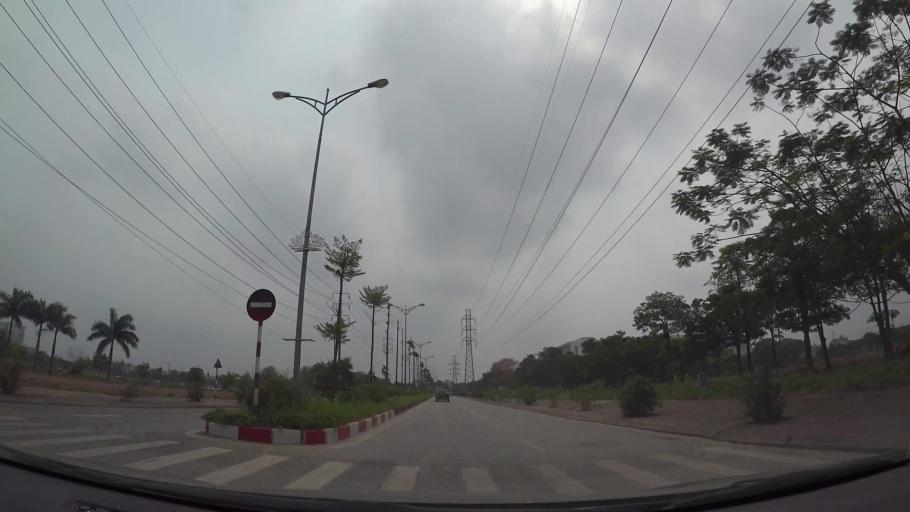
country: VN
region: Ha Noi
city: Trau Quy
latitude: 21.0641
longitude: 105.9043
